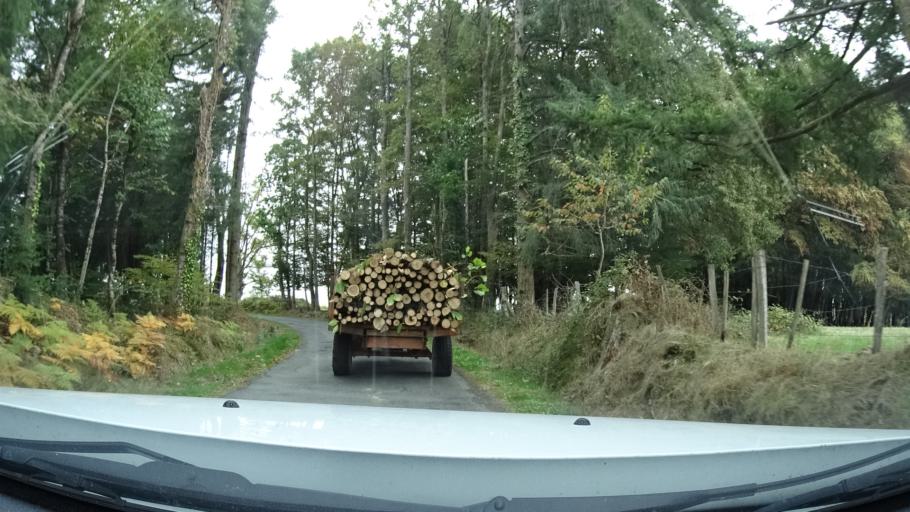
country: FR
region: Aquitaine
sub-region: Departement de la Dordogne
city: La Coquille
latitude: 45.4895
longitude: 0.9718
